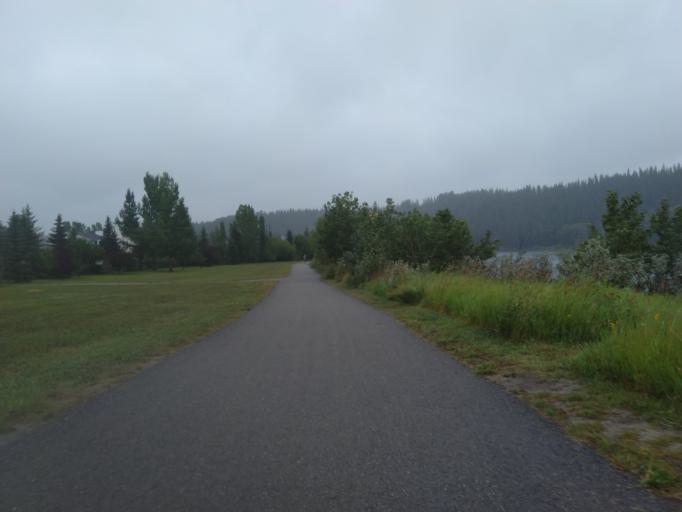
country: CA
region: Alberta
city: Cochrane
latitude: 51.1775
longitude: -114.4776
